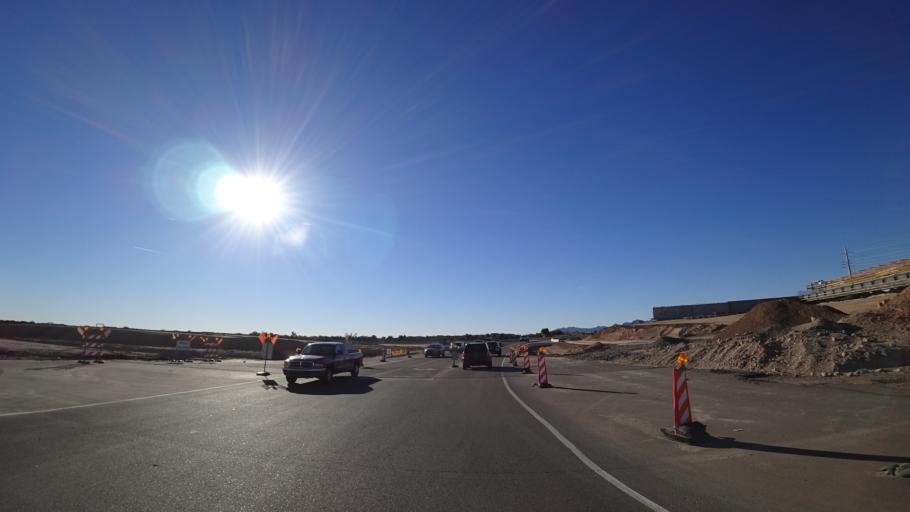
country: US
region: Arizona
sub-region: Maricopa County
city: Goodyear
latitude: 33.4493
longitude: -112.4265
